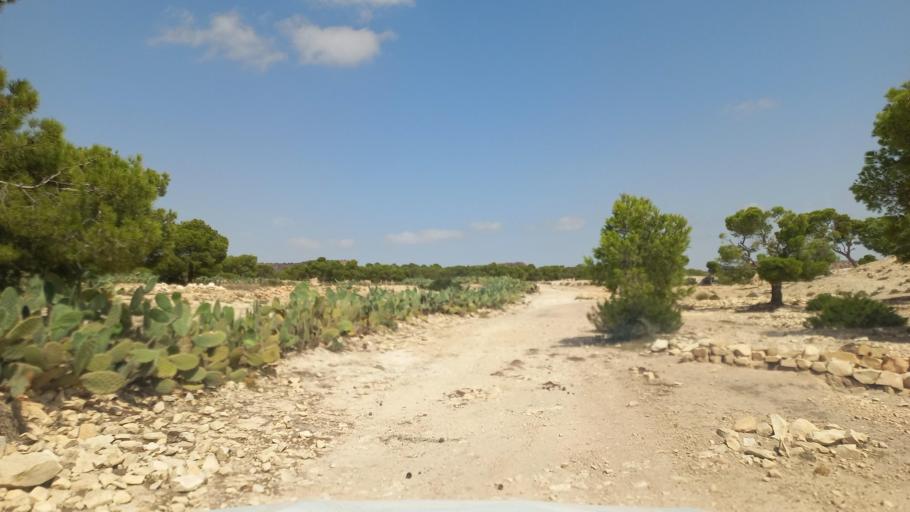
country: TN
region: Al Qasrayn
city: Sbiba
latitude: 35.4044
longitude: 8.9698
